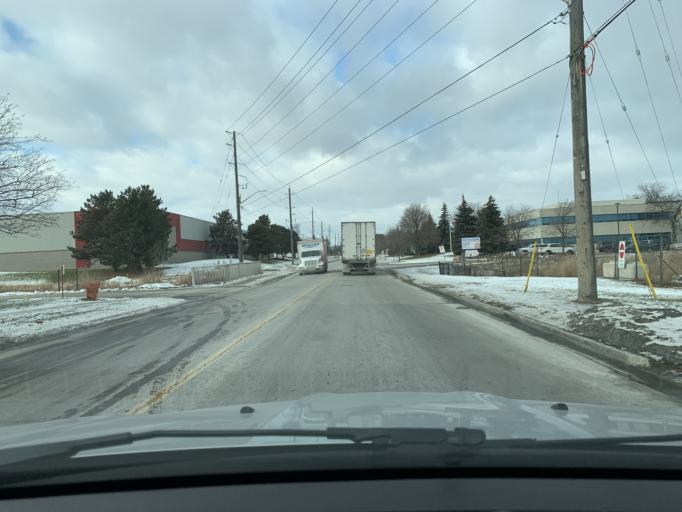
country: CA
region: Ontario
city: Brampton
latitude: 43.7270
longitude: -79.6798
